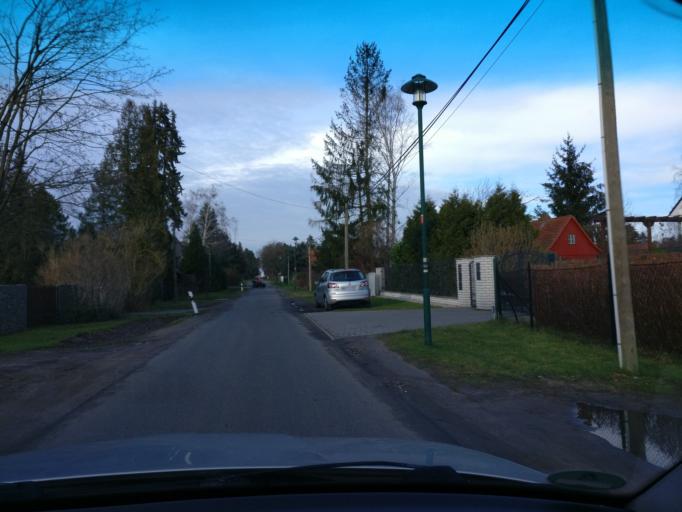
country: DE
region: Brandenburg
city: Bernau bei Berlin
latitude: 52.6697
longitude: 13.5418
